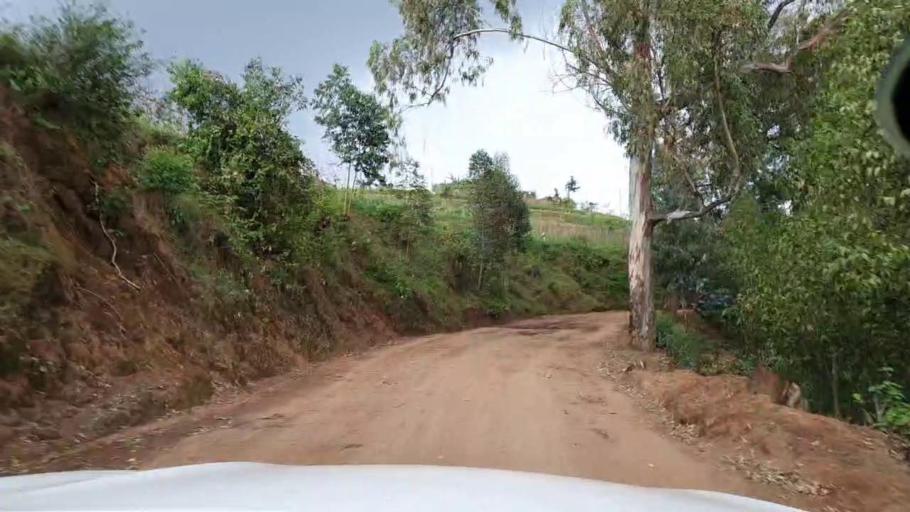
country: BI
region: Kayanza
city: Kayanza
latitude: -2.7894
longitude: 29.5262
